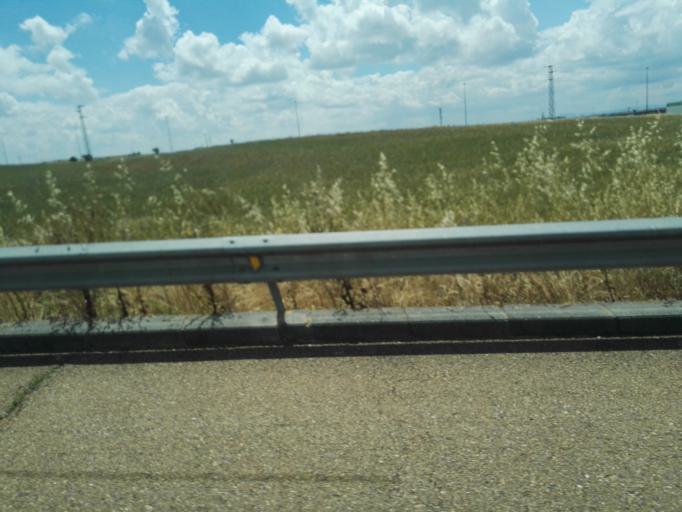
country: ES
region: Extremadura
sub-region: Provincia de Badajoz
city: Badajoz
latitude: 38.9054
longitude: -6.9974
